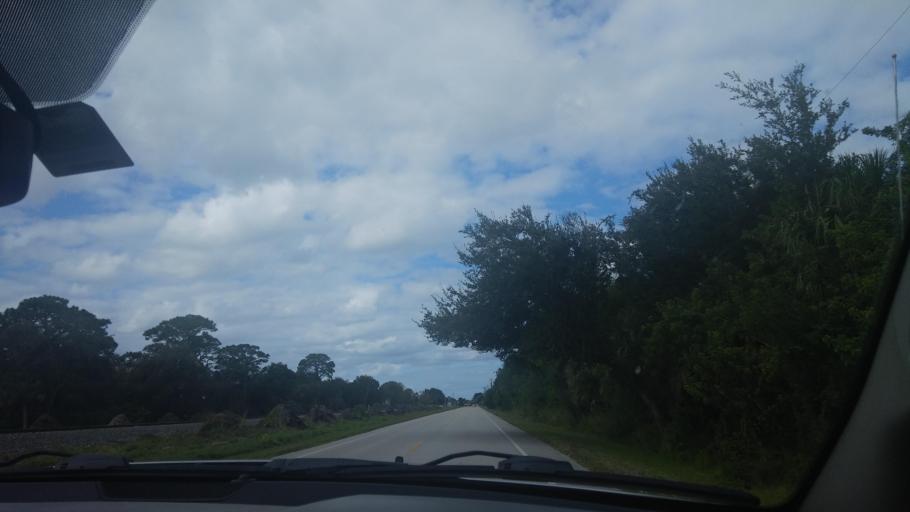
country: US
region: Florida
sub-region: Indian River County
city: Winter Beach
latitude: 27.7301
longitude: -80.4273
